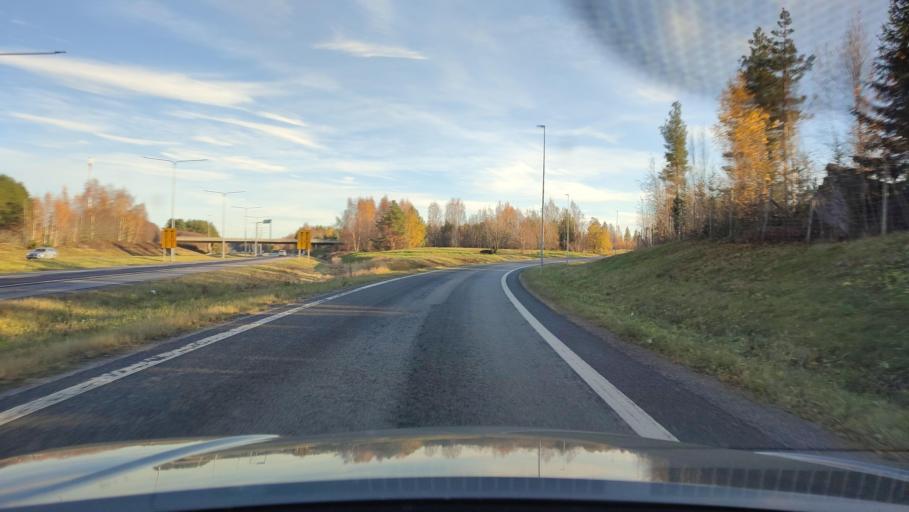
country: FI
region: Ostrobothnia
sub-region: Vaasa
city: Ristinummi
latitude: 63.0301
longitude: 21.7516
